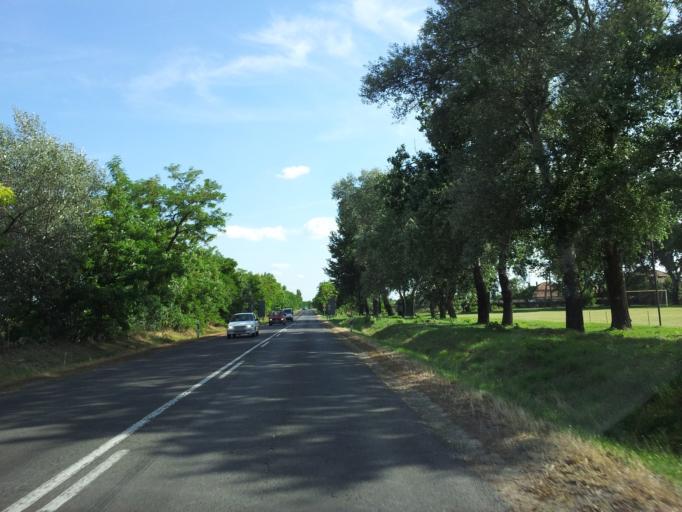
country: HU
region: Pest
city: Kiskunlachaza
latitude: 47.2337
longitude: 19.0209
